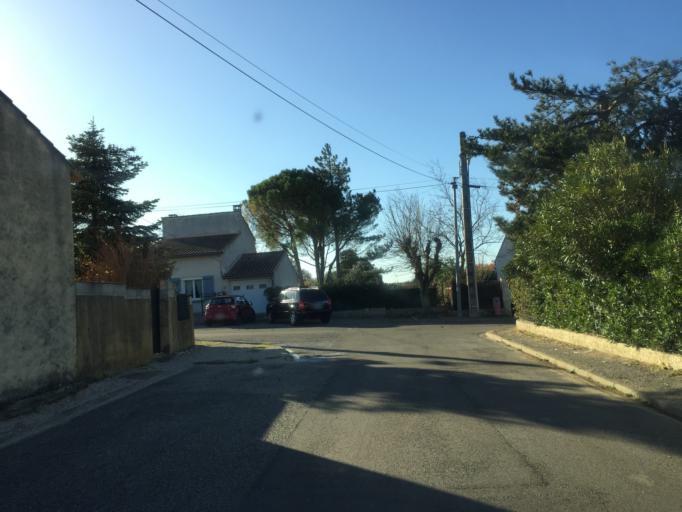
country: FR
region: Provence-Alpes-Cote d'Azur
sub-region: Departement du Vaucluse
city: Bedarrides
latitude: 44.0353
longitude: 4.8924
